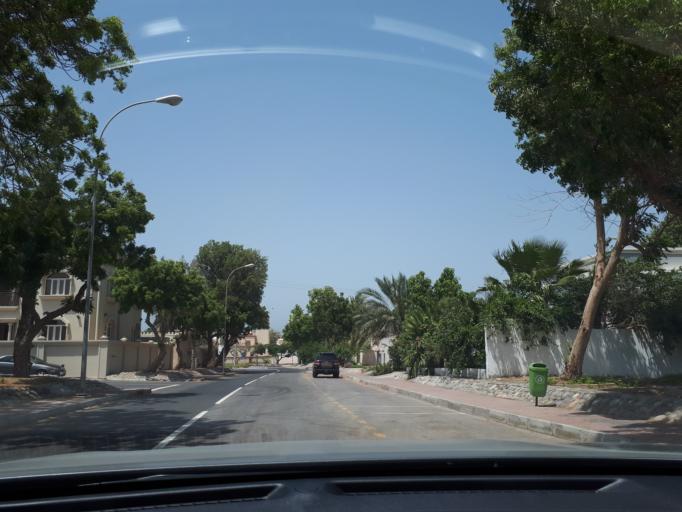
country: OM
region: Muhafazat Masqat
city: As Sib al Jadidah
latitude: 23.7086
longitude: 58.0746
